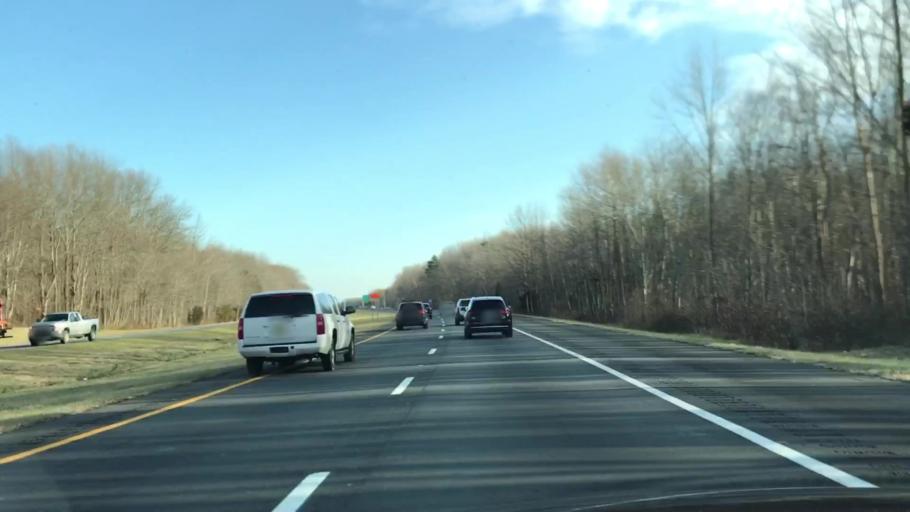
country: US
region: New Jersey
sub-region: Monmouth County
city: Shrewsbury
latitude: 40.1642
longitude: -74.4364
